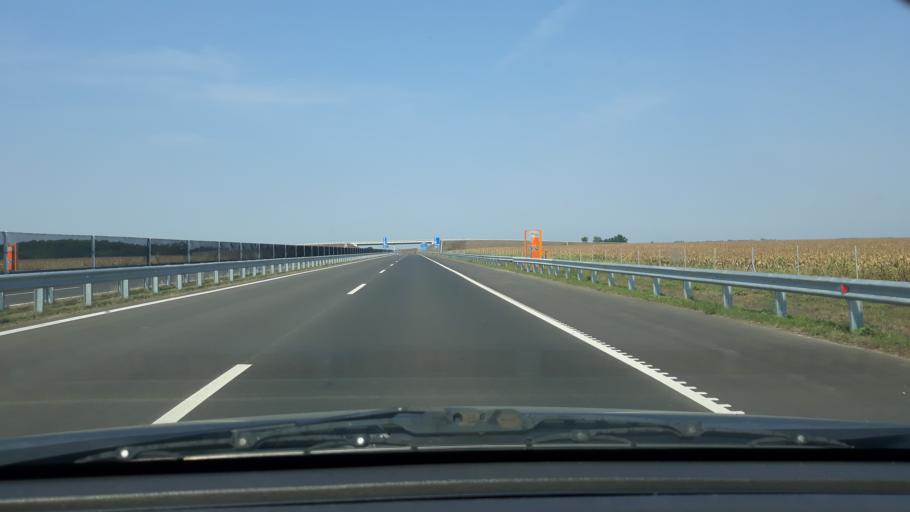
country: HU
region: Hajdu-Bihar
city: Berettyoujfalu
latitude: 47.2598
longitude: 21.5667
